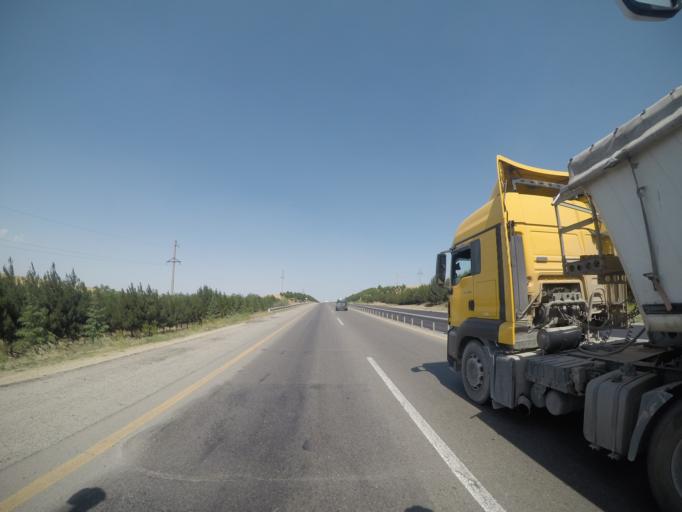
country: AZ
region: Haciqabul
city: Haciqabul
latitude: 40.0450
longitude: 48.9743
